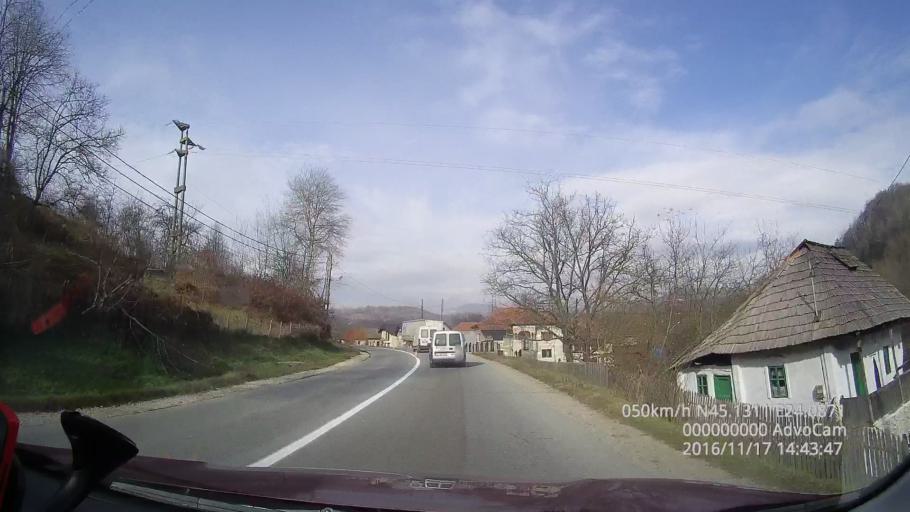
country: RO
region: Valcea
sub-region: Comuna Pietrari
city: Pietrarii de Sus
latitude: 45.1314
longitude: 24.0870
